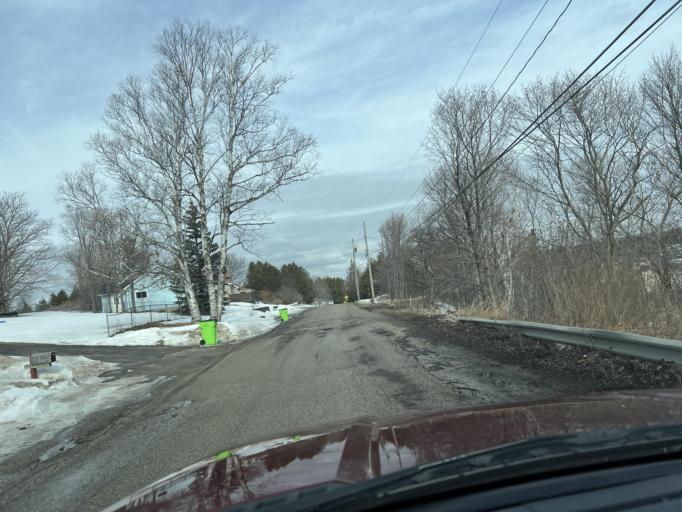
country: US
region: Michigan
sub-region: Mackinac County
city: Saint Ignace
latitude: 45.8698
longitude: -84.7337
